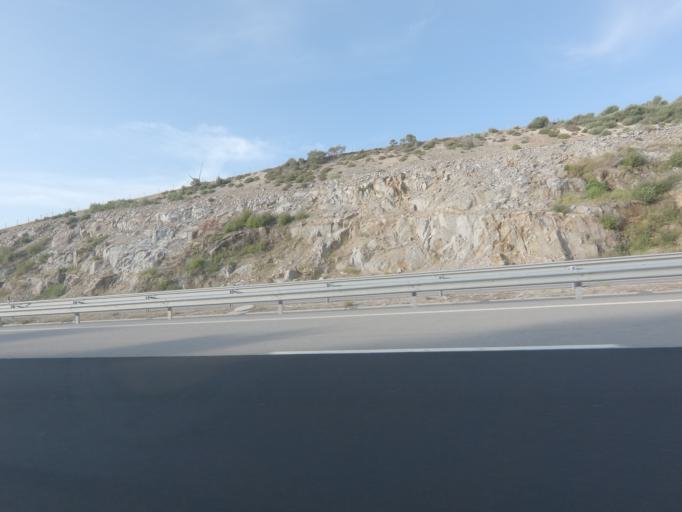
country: PT
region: Vila Real
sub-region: Vila Pouca de Aguiar
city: Vila Pouca de Aguiar
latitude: 41.4419
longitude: -7.6448
